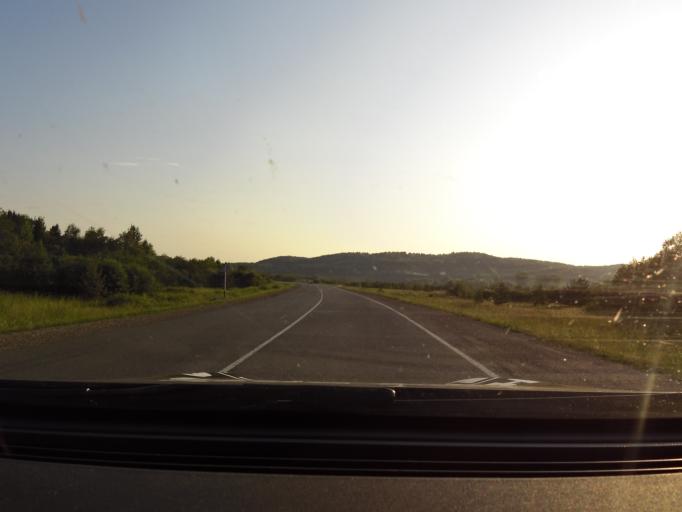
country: RU
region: Sverdlovsk
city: Mikhaylovsk
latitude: 56.4565
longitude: 59.0950
